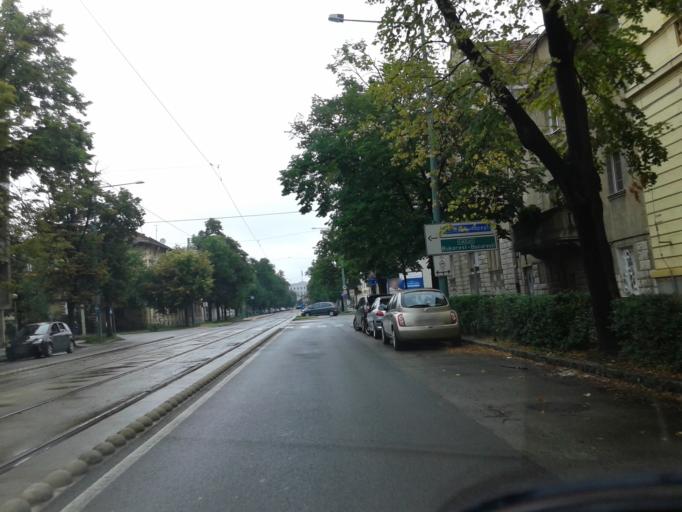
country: HU
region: Csongrad
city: Szeged
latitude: 46.2426
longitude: 20.1432
